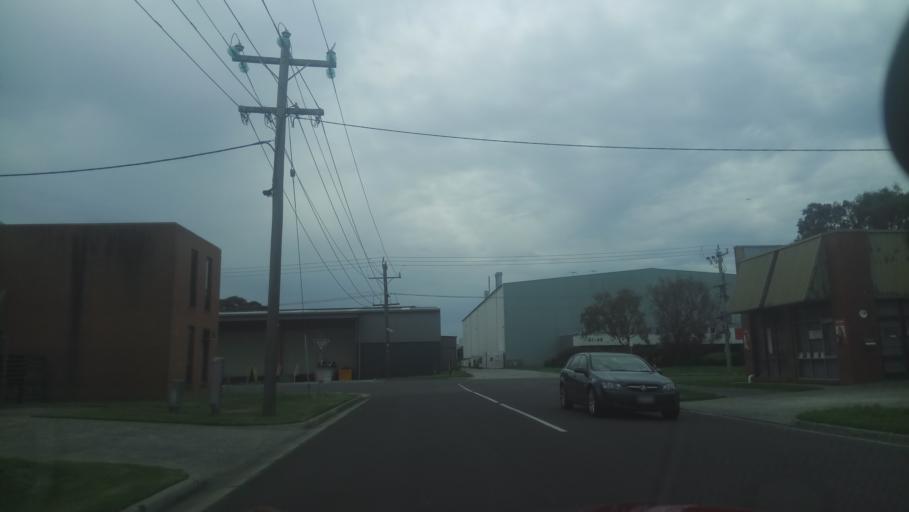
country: AU
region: Victoria
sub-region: Kingston
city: Aspendale Gardens
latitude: -38.0018
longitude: 145.1123
